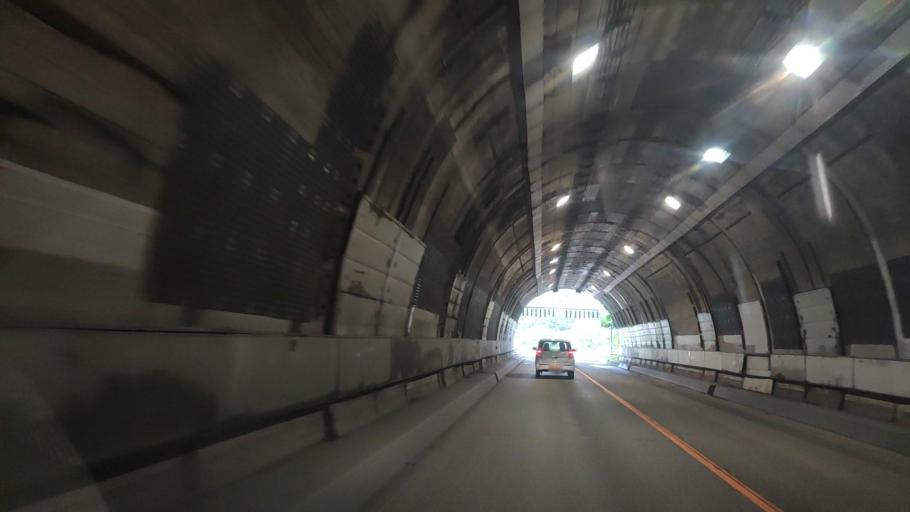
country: JP
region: Hokkaido
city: Date
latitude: 42.5719
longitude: 140.7326
